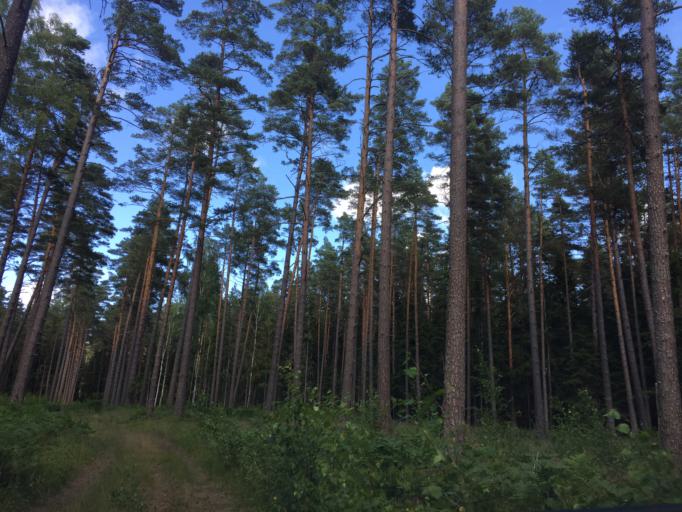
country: LV
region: Ventspils
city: Ventspils
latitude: 57.4736
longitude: 21.6564
